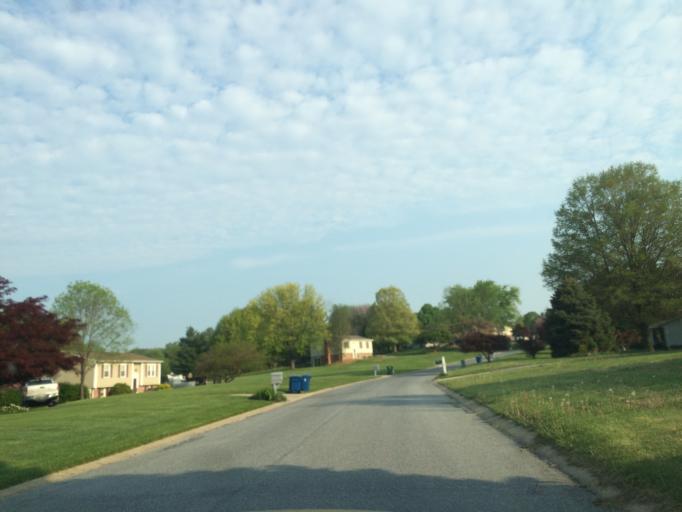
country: US
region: Maryland
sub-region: Carroll County
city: Sykesville
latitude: 39.3938
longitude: -77.0294
